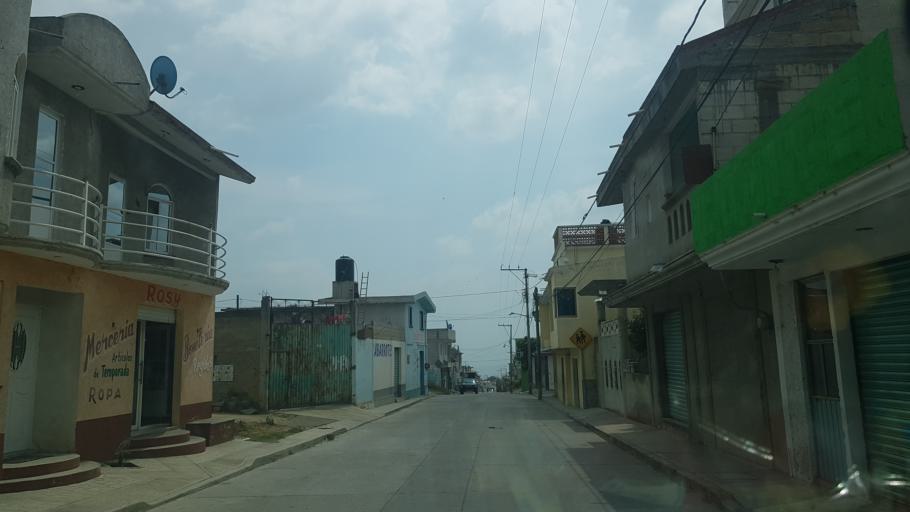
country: MX
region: Puebla
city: Domingo Arenas
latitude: 19.1358
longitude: -98.4912
